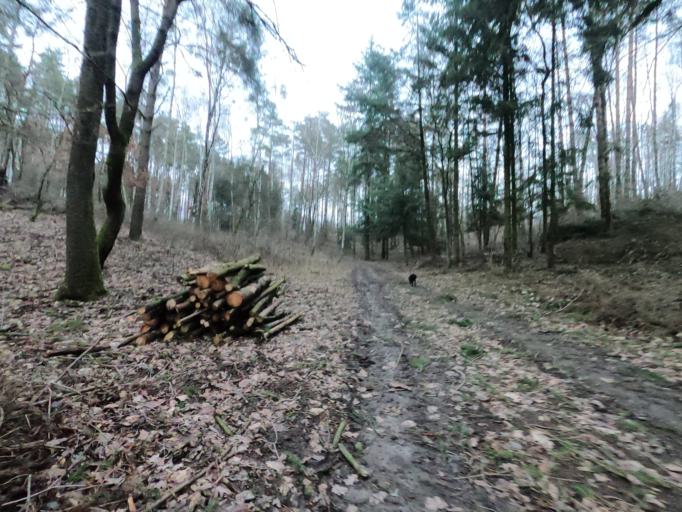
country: PL
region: Greater Poland Voivodeship
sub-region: Powiat pilski
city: Wyrzysk
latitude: 53.1172
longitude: 17.2147
